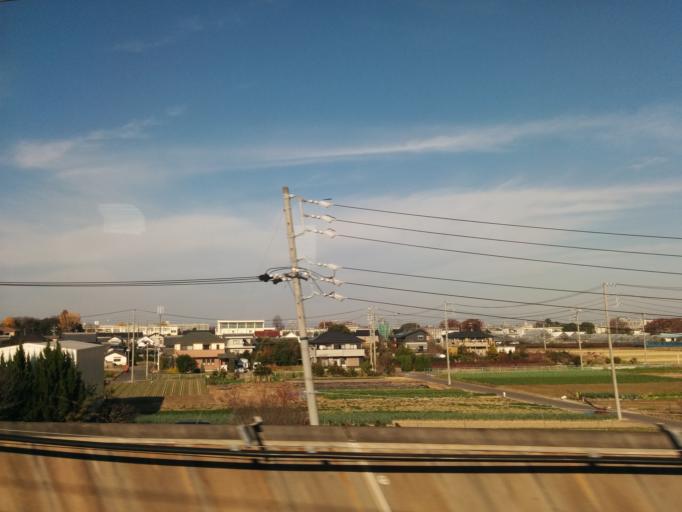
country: JP
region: Aichi
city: Inazawa
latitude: 35.2366
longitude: 136.7865
